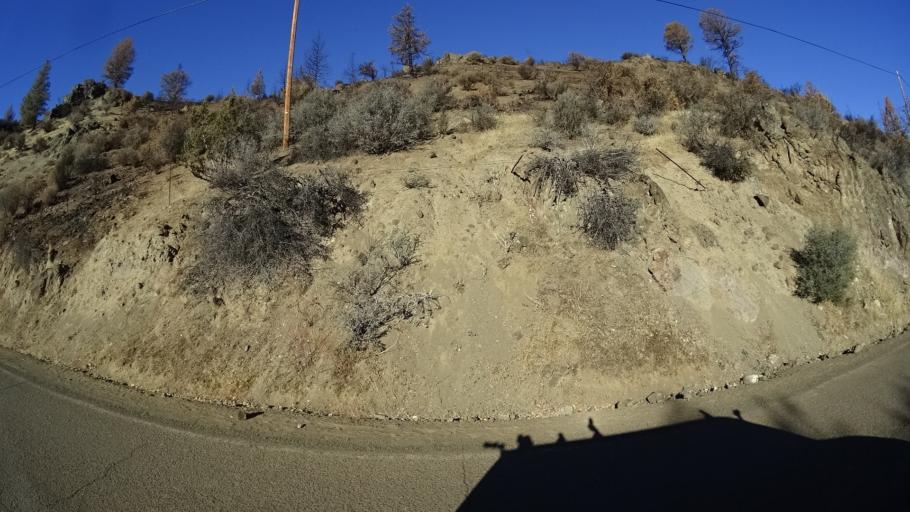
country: US
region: California
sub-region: Siskiyou County
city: Montague
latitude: 41.9158
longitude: -122.4618
